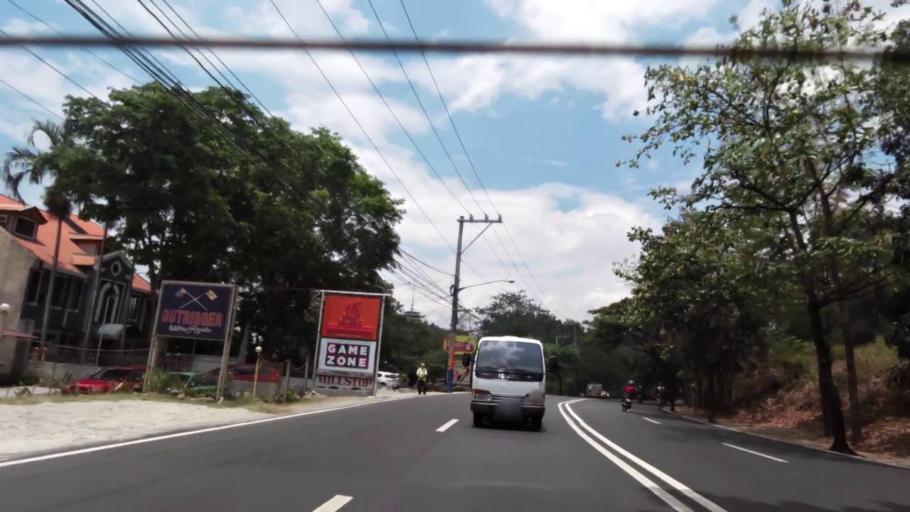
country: PH
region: Calabarzon
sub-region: Province of Rizal
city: Antipolo
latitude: 14.6121
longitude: 121.1573
